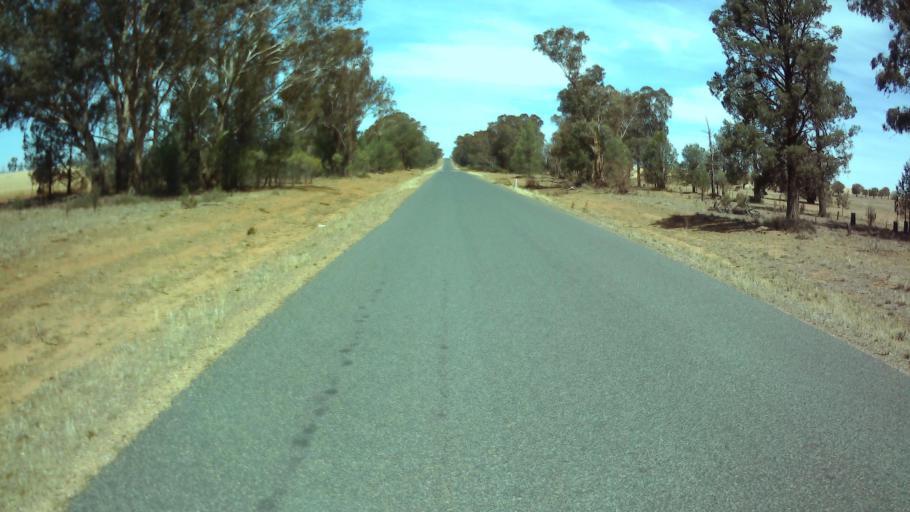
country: AU
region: New South Wales
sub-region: Weddin
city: Grenfell
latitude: -33.8951
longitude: 147.7488
